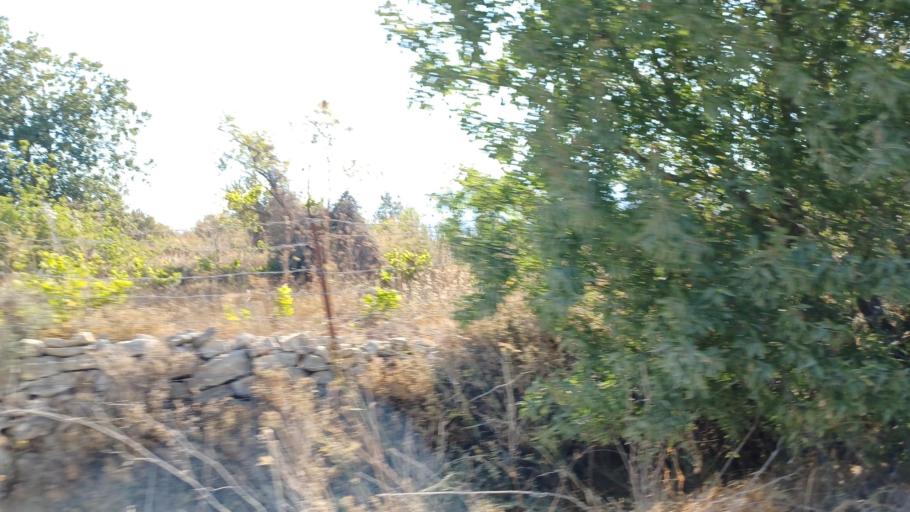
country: CY
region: Limassol
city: Pachna
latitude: 34.8430
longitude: 32.7129
